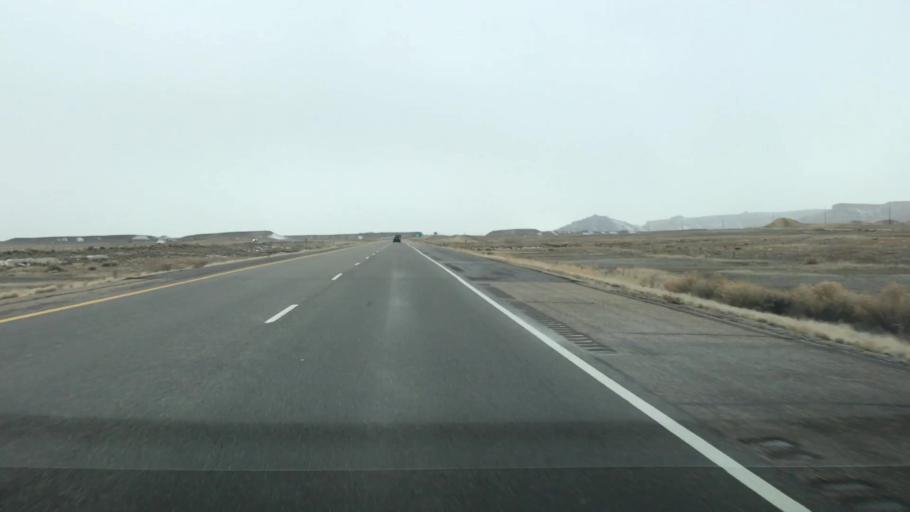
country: US
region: Utah
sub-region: Grand County
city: Moab
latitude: 38.9476
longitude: -109.7908
